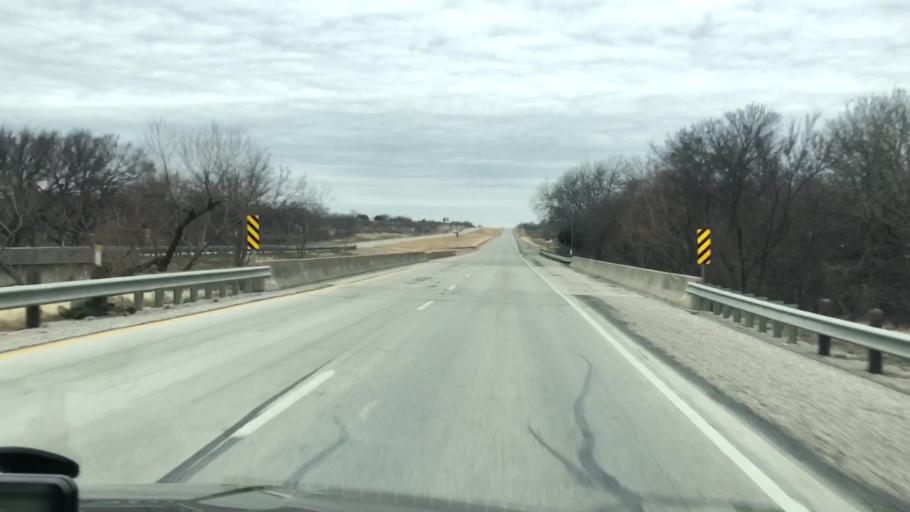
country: US
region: Texas
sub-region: Jack County
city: Jacksboro
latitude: 33.2403
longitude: -98.2175
